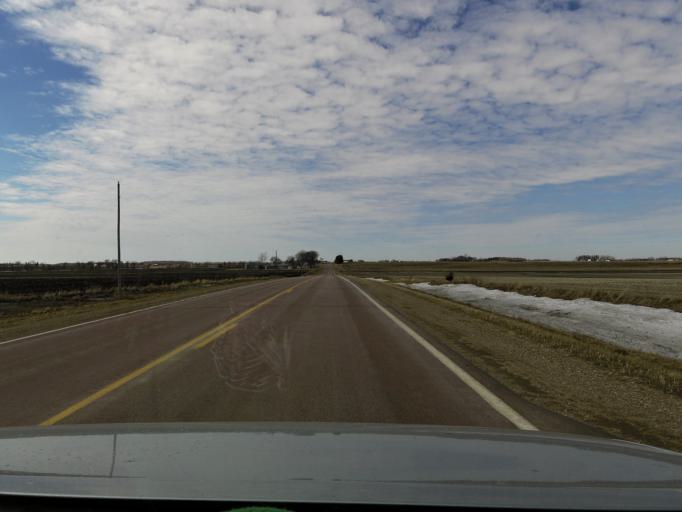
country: US
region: Minnesota
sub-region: Le Sueur County
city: Montgomery
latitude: 44.4860
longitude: -93.6616
